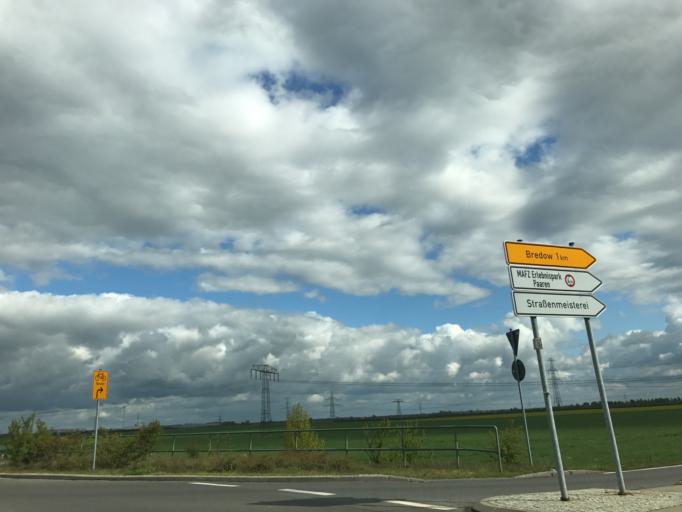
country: DE
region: Brandenburg
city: Nauen
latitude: 52.5790
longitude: 12.9084
